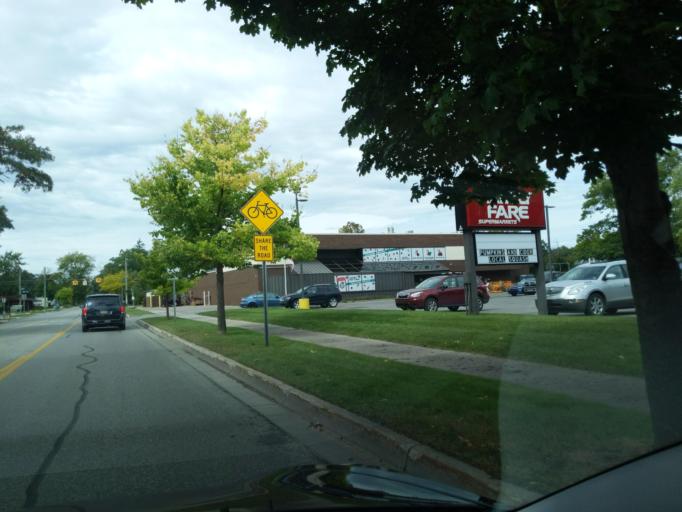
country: US
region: Michigan
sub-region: Grand Traverse County
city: Traverse City
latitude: 44.7589
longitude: -85.5989
